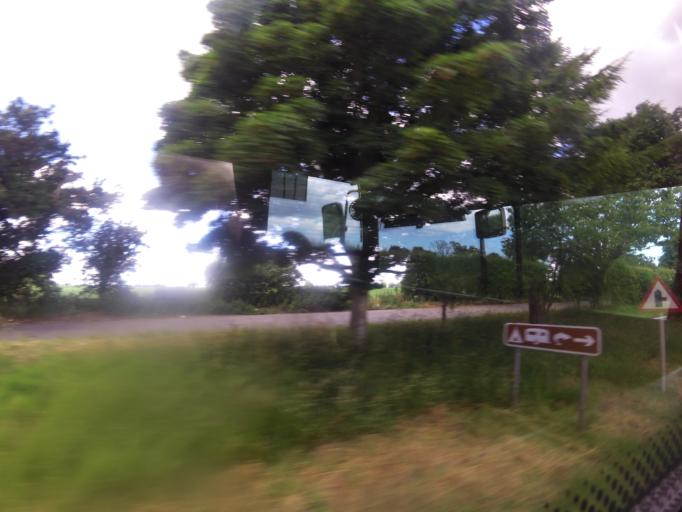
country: GB
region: England
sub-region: Norfolk
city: Aylsham
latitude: 52.8584
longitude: 1.2825
